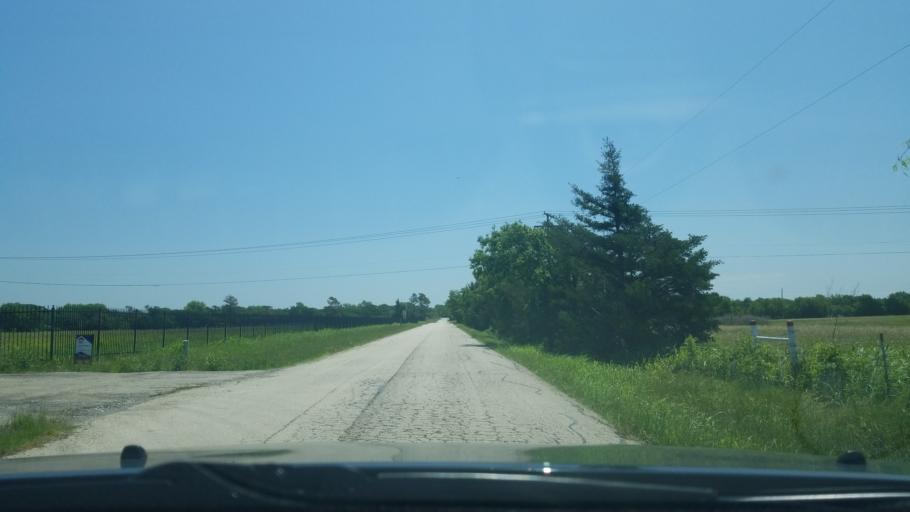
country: US
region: Texas
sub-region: Denton County
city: Krum
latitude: 33.2442
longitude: -97.2479
